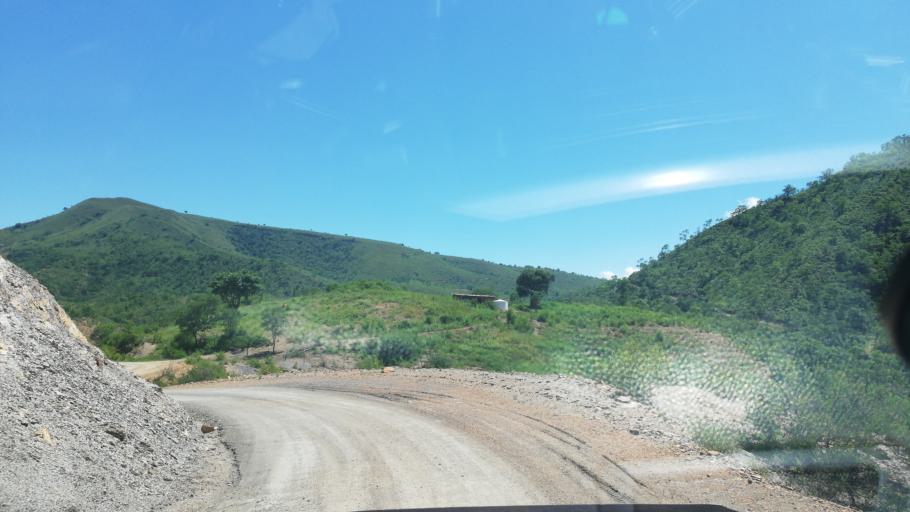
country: BO
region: Cochabamba
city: Mizque
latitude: -17.8416
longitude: -65.3090
